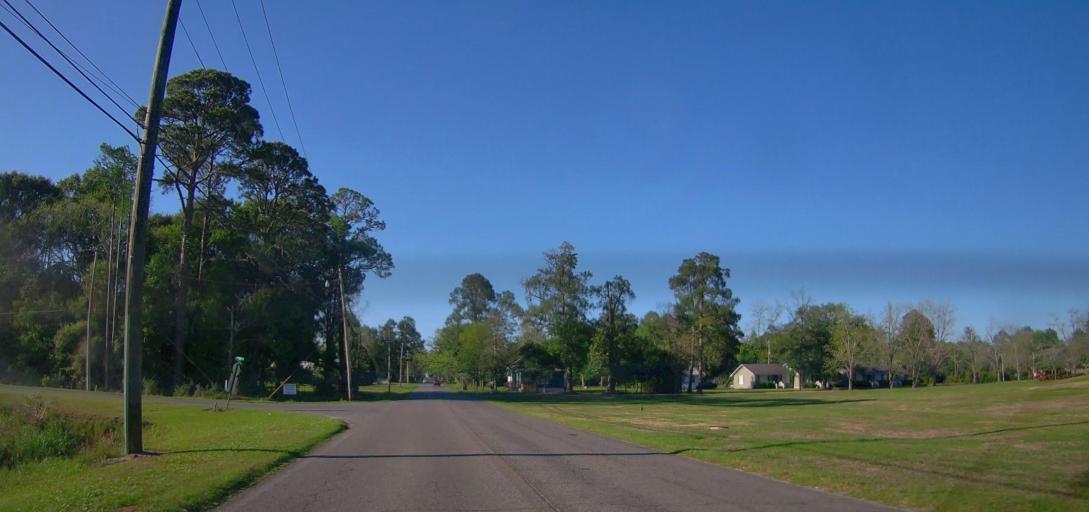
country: US
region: Georgia
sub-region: Ben Hill County
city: Fitzgerald
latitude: 31.7106
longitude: -83.2648
